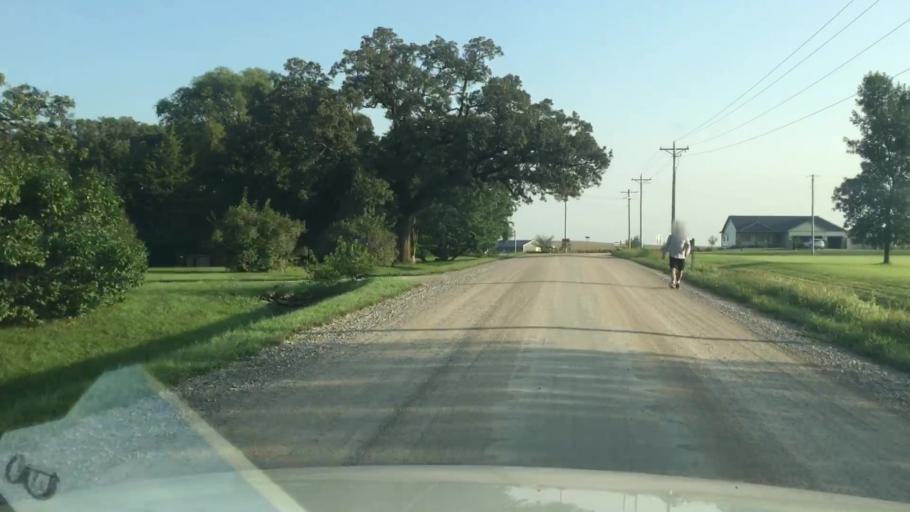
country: US
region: Iowa
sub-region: Story County
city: Huxley
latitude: 41.9165
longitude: -93.5766
